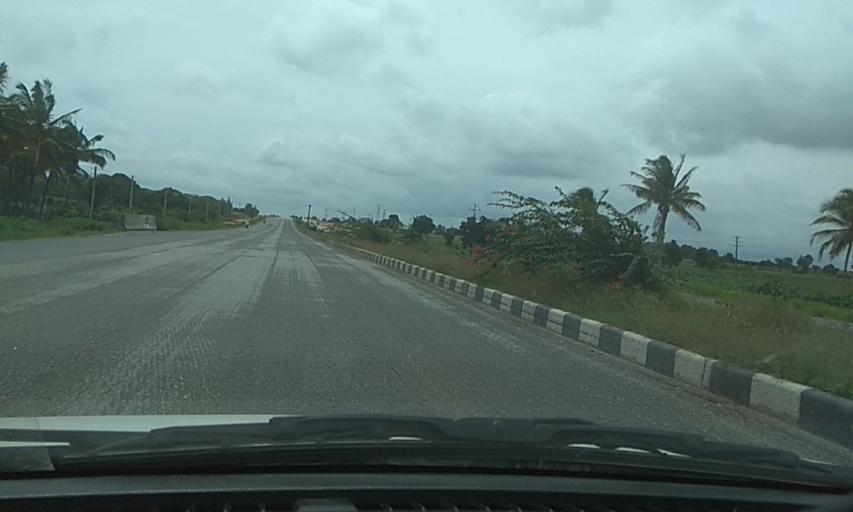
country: IN
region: Karnataka
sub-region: Davanagere
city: Mayakonda
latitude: 14.3322
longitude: 76.2184
